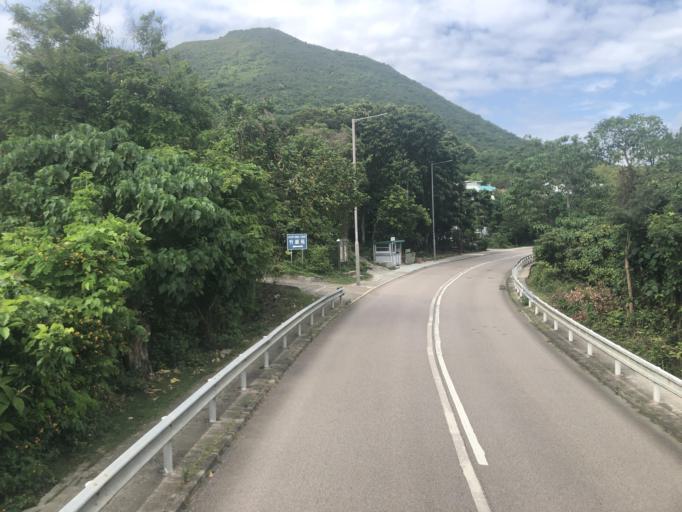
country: HK
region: Sai Kung
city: Sai Kung
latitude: 22.3919
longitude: 114.3082
